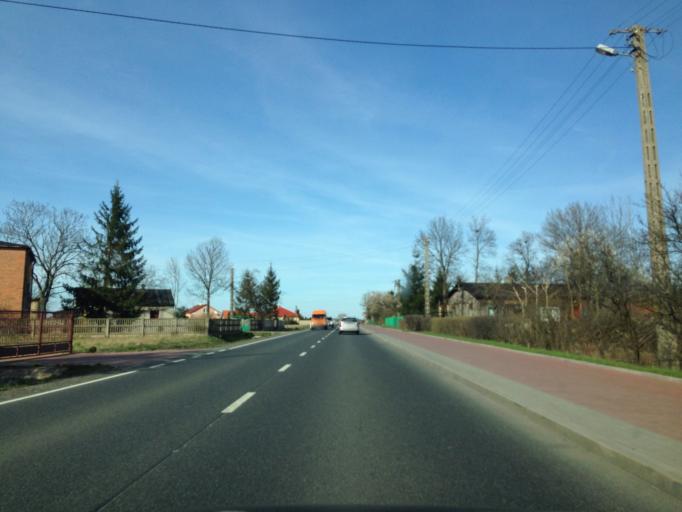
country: PL
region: Lodz Voivodeship
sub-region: Powiat poddebicki
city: Wartkowice
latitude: 51.9875
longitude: 19.0356
